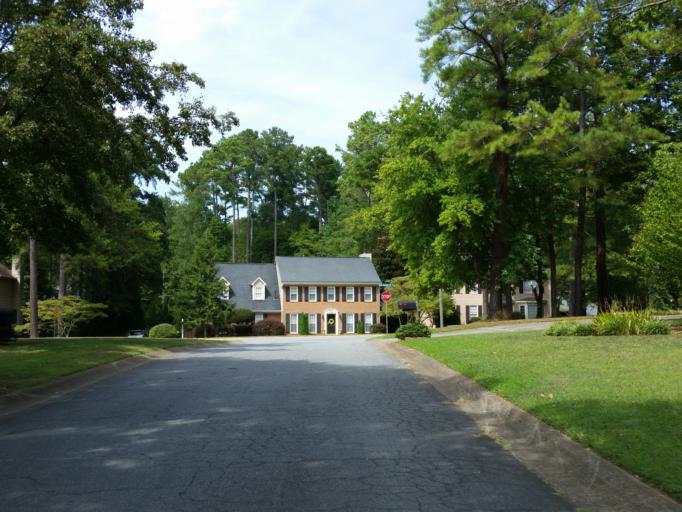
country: US
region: Georgia
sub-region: Cherokee County
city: Woodstock
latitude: 34.0279
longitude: -84.5126
